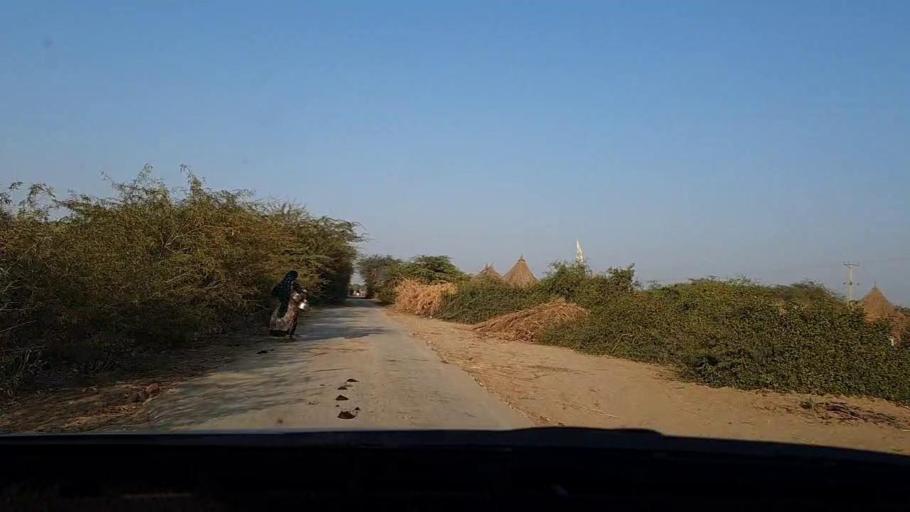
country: PK
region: Sindh
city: Tando Mittha Khan
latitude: 25.8696
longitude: 69.3098
